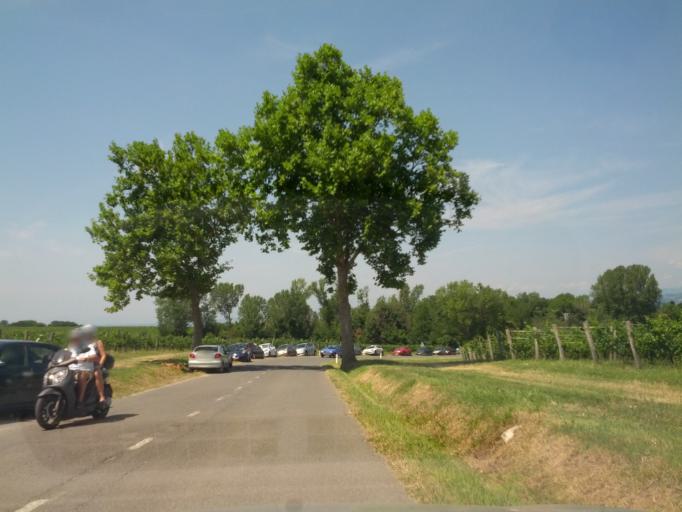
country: SI
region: Koper-Capodistria
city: Ankaran
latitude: 45.5887
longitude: 13.7124
